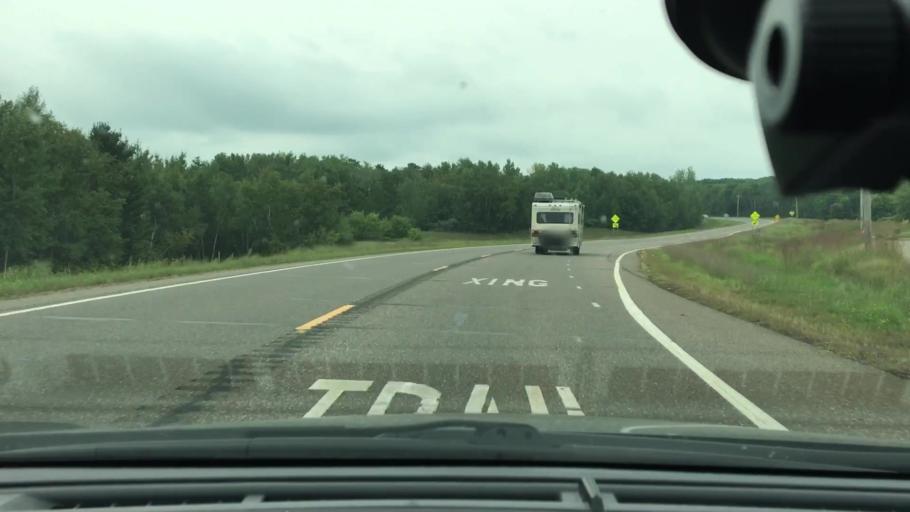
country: US
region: Minnesota
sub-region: Crow Wing County
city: Crosby
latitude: 46.4924
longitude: -93.9558
